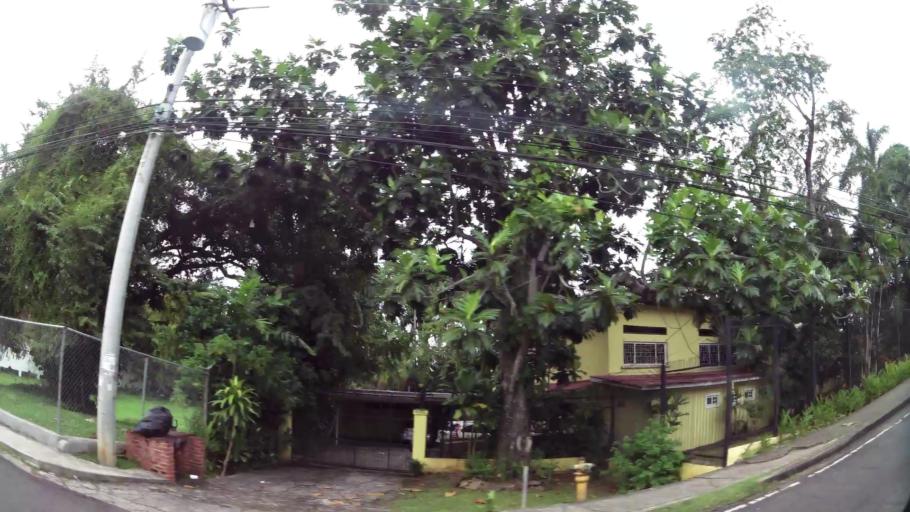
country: PA
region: Panama
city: Panama
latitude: 9.0018
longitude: -79.5011
